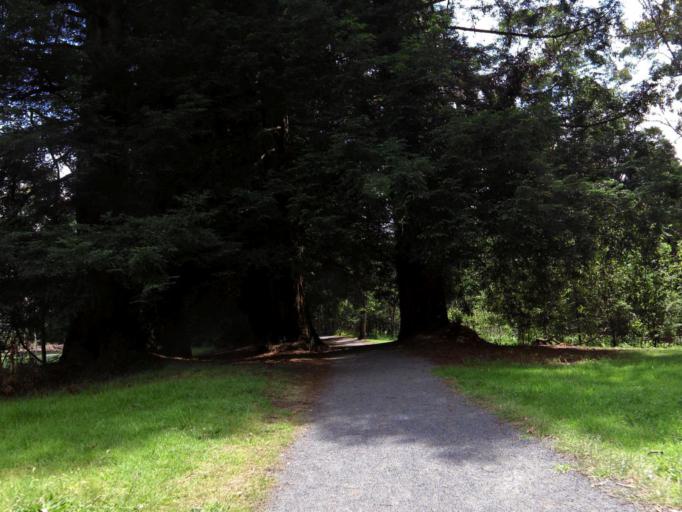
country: AU
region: Victoria
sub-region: Yarra Ranges
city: Millgrove
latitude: -37.7506
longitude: 145.7006
